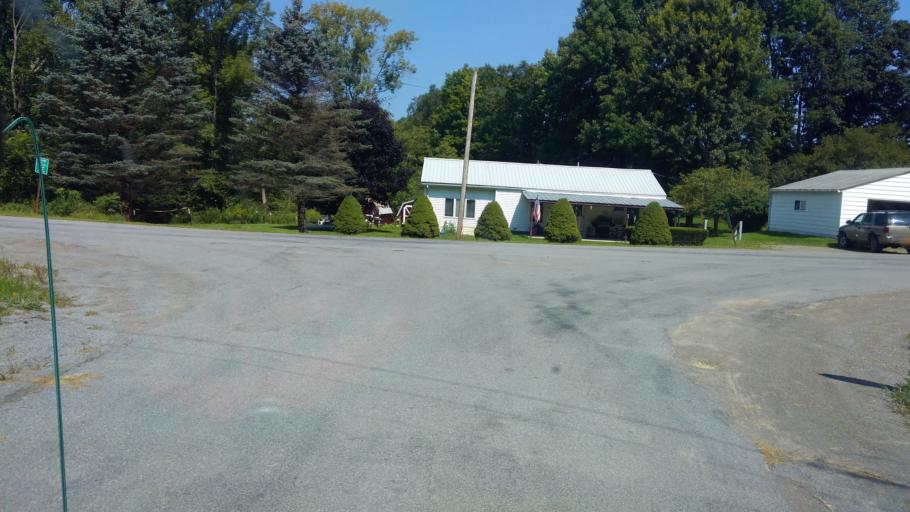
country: US
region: New York
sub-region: Allegany County
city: Houghton
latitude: 42.3424
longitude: -78.0741
